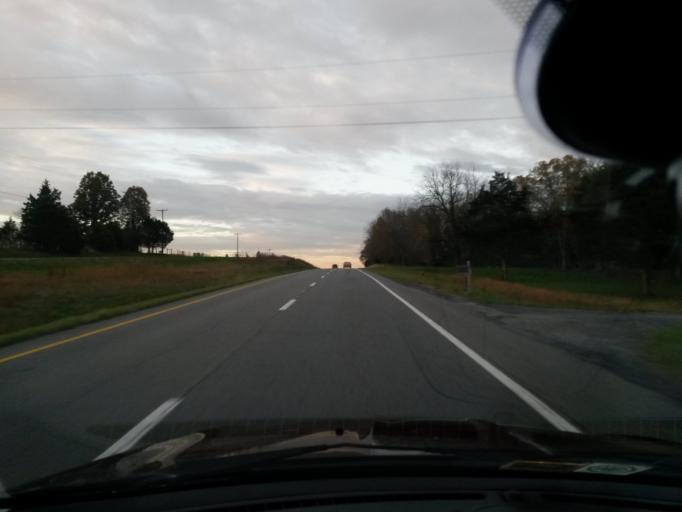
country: US
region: Virginia
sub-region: Botetourt County
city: Fincastle
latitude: 37.5415
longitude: -79.8628
